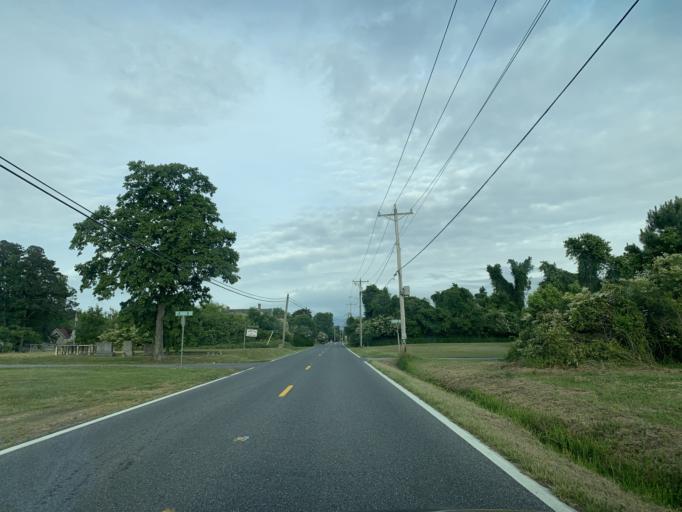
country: US
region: Virginia
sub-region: Accomack County
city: Captains Cove
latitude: 38.0562
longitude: -75.4158
